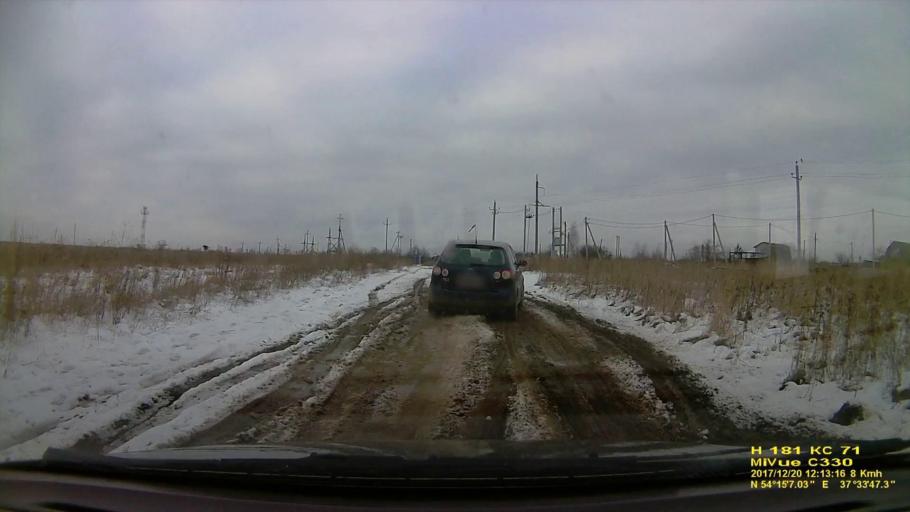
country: RU
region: Tula
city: Gorelki
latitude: 54.2520
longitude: 37.5632
